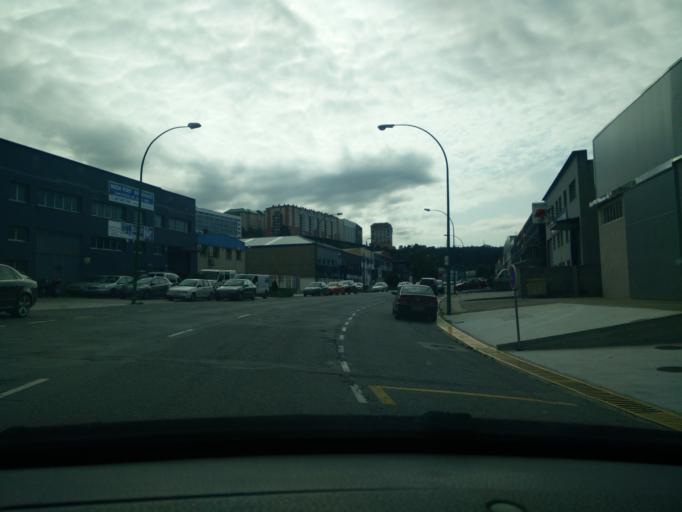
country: ES
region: Galicia
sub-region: Provincia da Coruna
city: A Coruna
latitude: 43.3278
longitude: -8.4341
